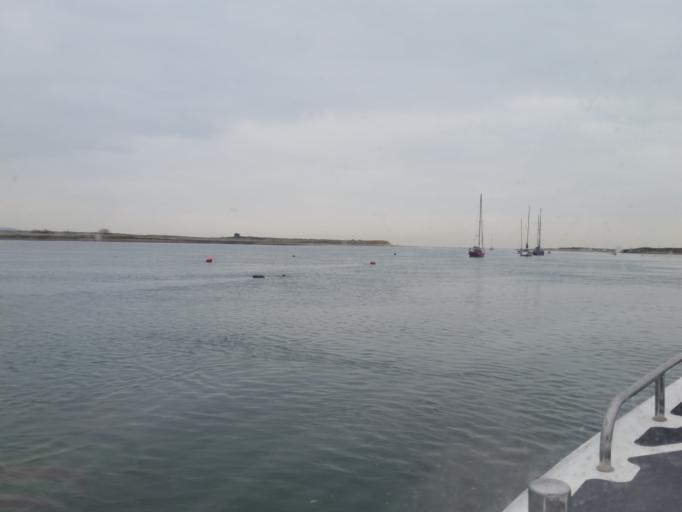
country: IE
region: Leinster
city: Malahide
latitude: 53.4536
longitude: -6.1498
